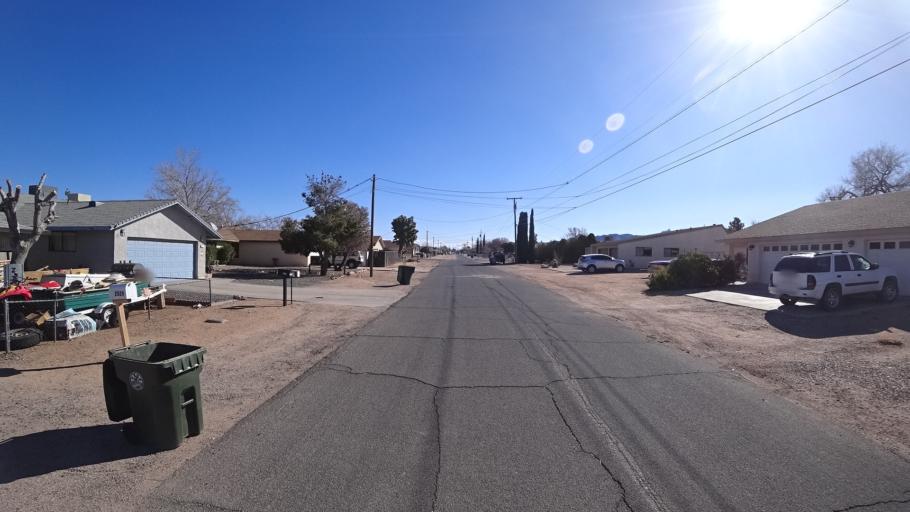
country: US
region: Arizona
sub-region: Mohave County
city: Kingman
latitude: 35.1972
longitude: -114.0189
